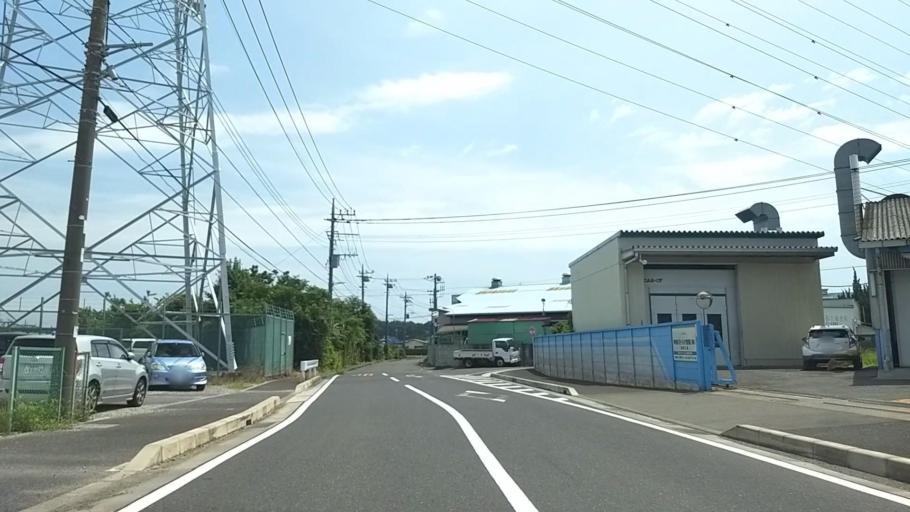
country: JP
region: Kanagawa
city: Minami-rinkan
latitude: 35.4237
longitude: 139.4296
